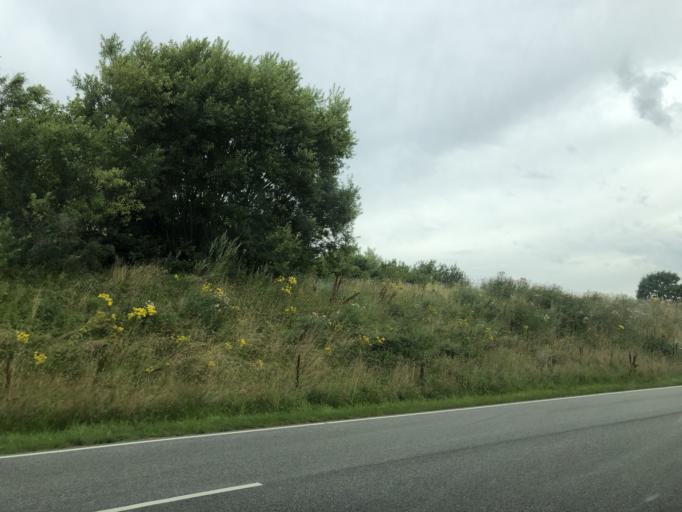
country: DK
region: Central Jutland
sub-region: Holstebro Kommune
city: Holstebro
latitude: 56.3853
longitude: 8.5956
